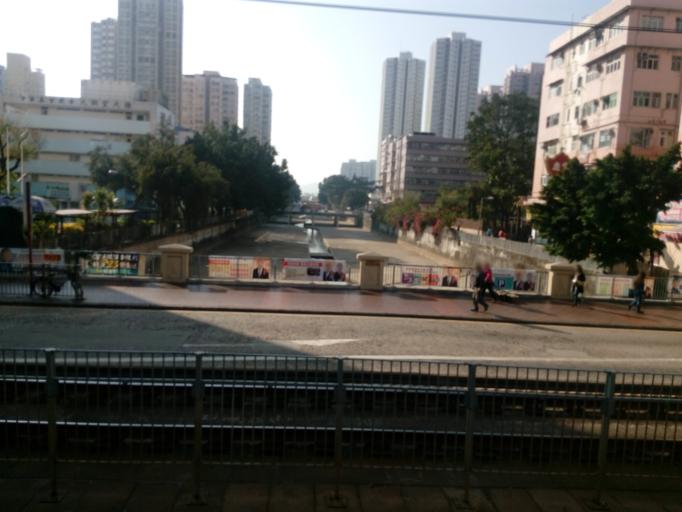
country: HK
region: Yuen Long
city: Yuen Long Kau Hui
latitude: 22.4444
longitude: 114.0256
